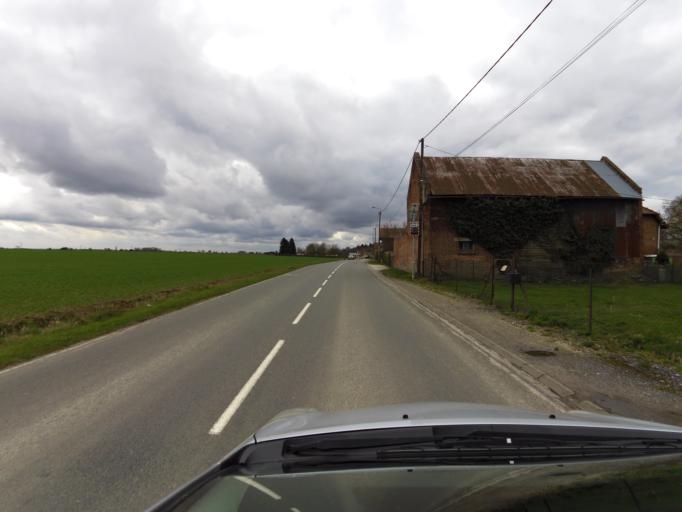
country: FR
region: Picardie
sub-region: Departement de la Somme
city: Chaulnes
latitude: 49.8870
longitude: 2.8093
